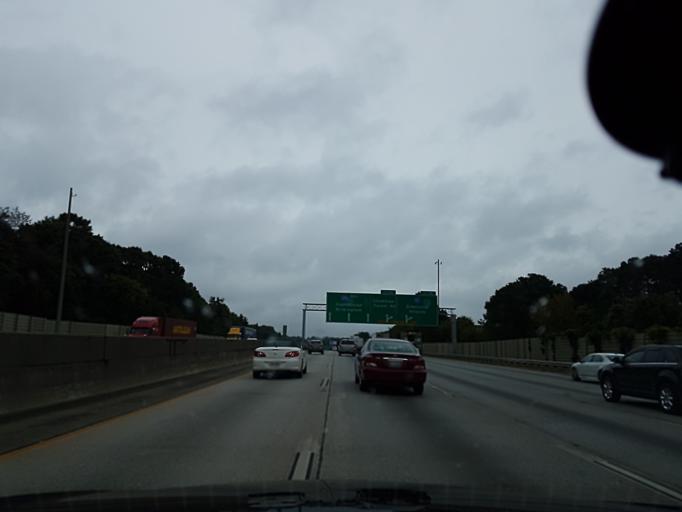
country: US
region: Georgia
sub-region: DeKalb County
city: Tucker
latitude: 33.8770
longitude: -84.2496
